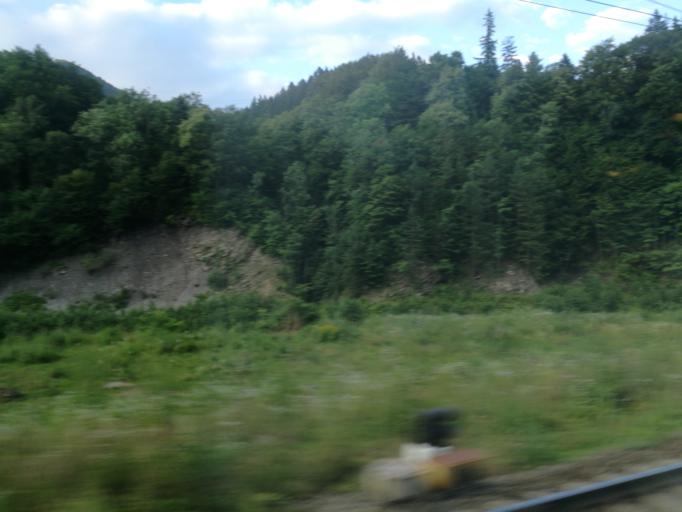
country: RO
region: Prahova
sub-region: Oras Sinaia
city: Sinaia
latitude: 45.3065
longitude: 25.5722
